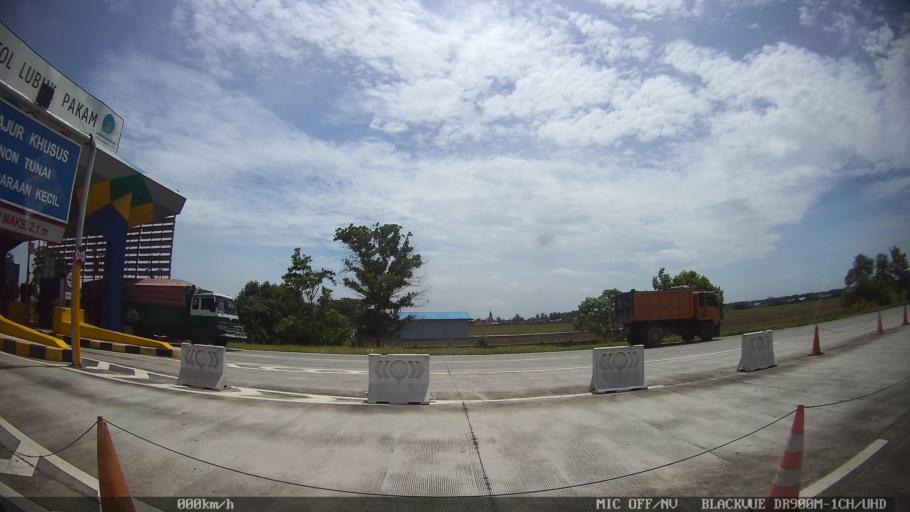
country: ID
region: North Sumatra
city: Perbaungan
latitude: 3.5379
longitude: 98.8925
